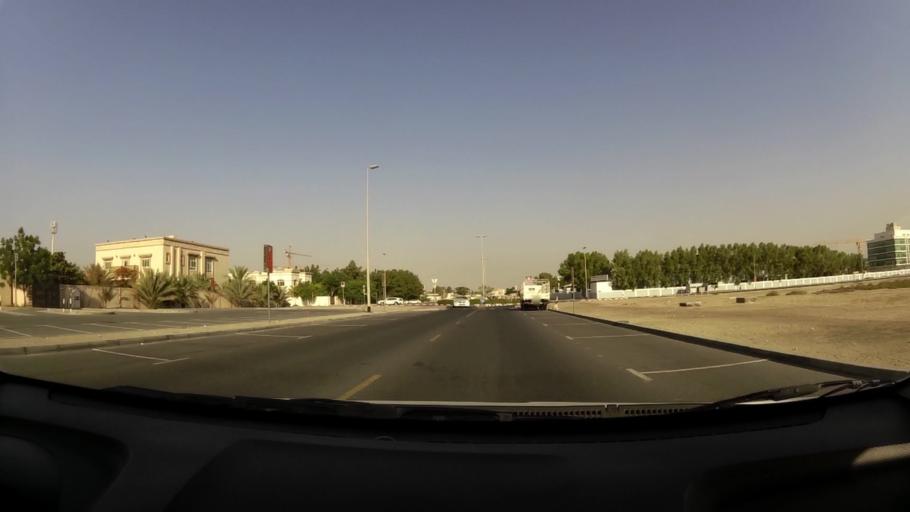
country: AE
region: Ash Shariqah
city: Sharjah
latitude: 25.2673
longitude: 55.3849
